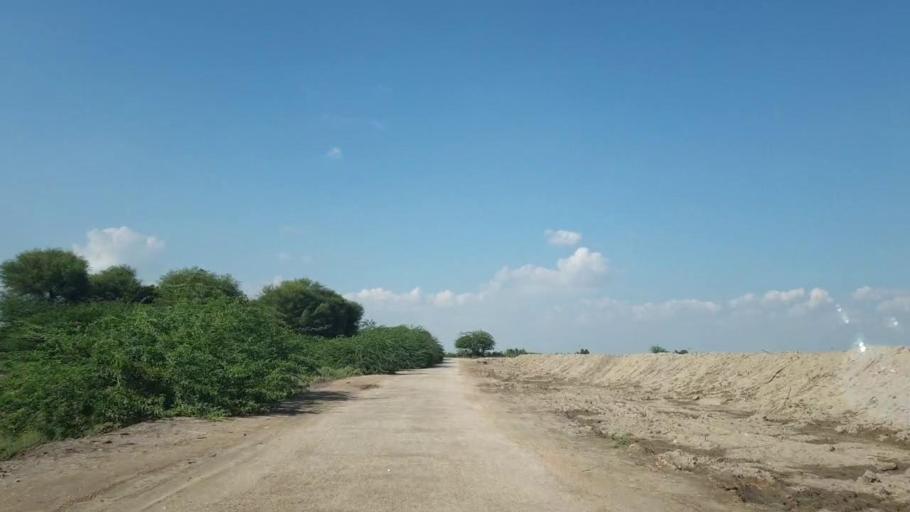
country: PK
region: Sindh
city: Pithoro
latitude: 25.6356
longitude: 69.4384
